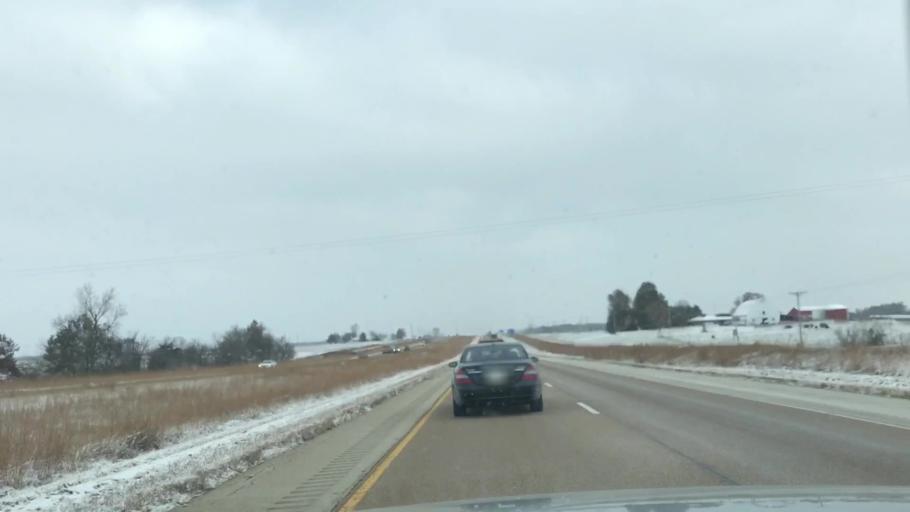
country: US
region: Illinois
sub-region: Montgomery County
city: Litchfield
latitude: 39.2481
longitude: -89.6412
